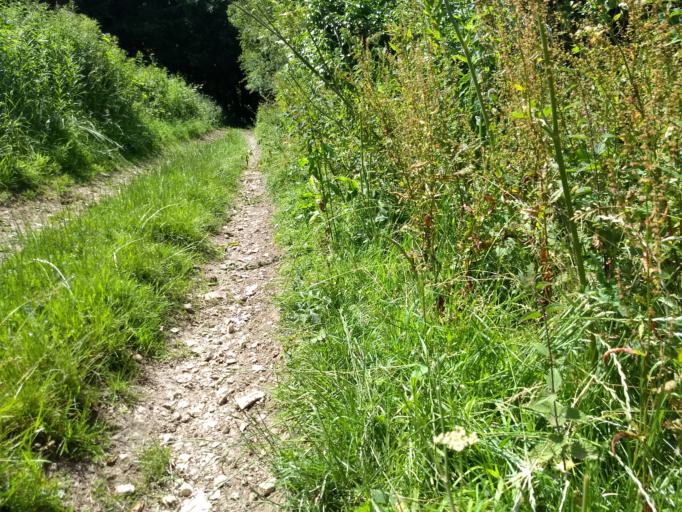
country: GB
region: England
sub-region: Isle of Wight
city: Shalfleet
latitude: 50.6649
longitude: -1.3808
